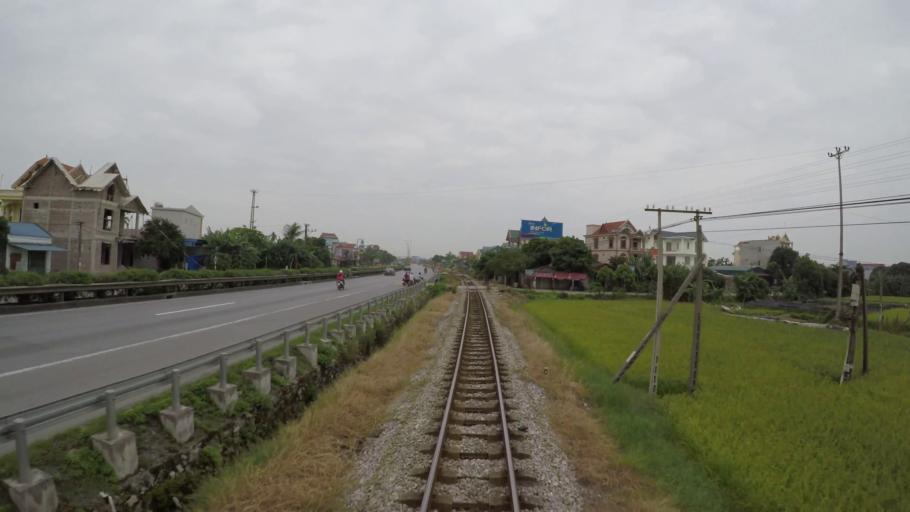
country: VN
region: Hai Duong
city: Phu Thai
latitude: 20.9547
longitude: 106.5286
